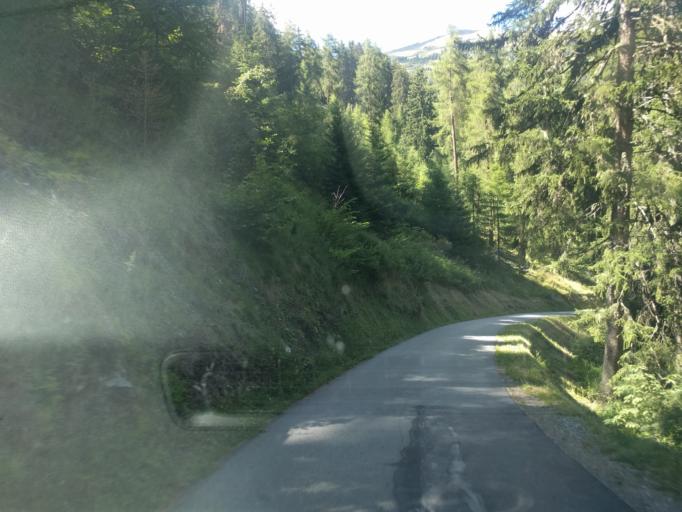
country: IT
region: Trentino-Alto Adige
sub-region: Bolzano
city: Tubre
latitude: 46.6115
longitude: 10.4206
